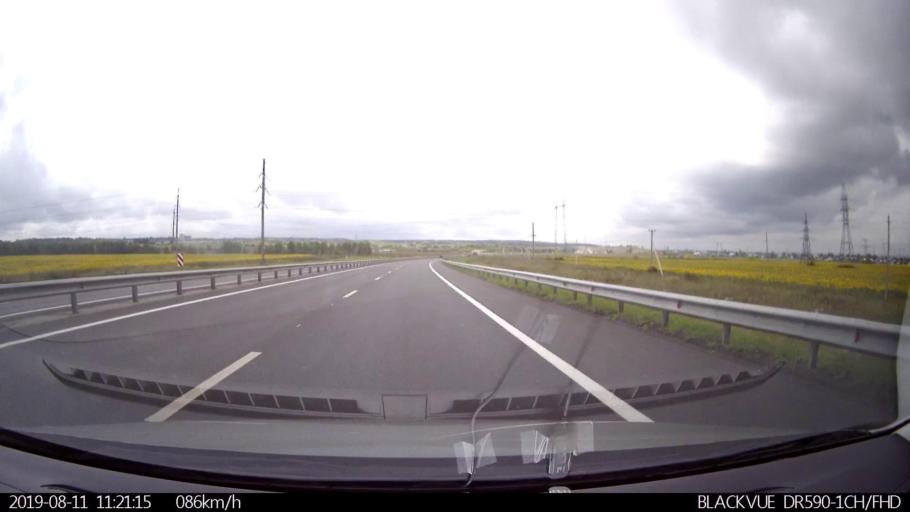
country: RU
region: Ulyanovsk
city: Novoul'yanovsk
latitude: 54.1482
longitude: 48.2641
